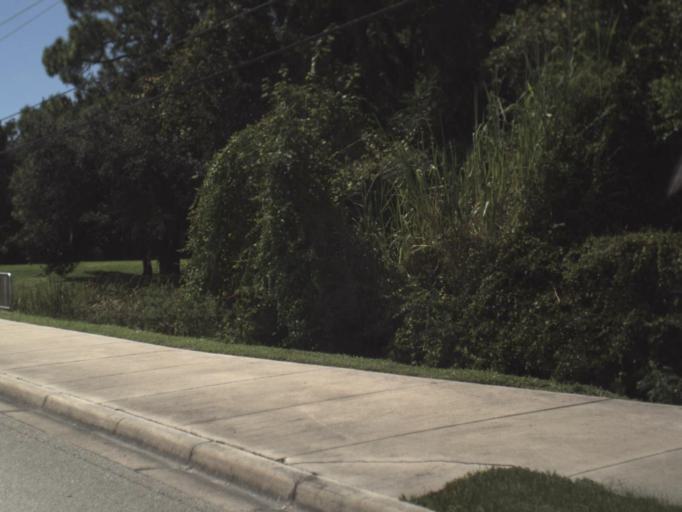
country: US
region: Florida
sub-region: Lee County
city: Suncoast Estates
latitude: 26.7089
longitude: -81.8394
